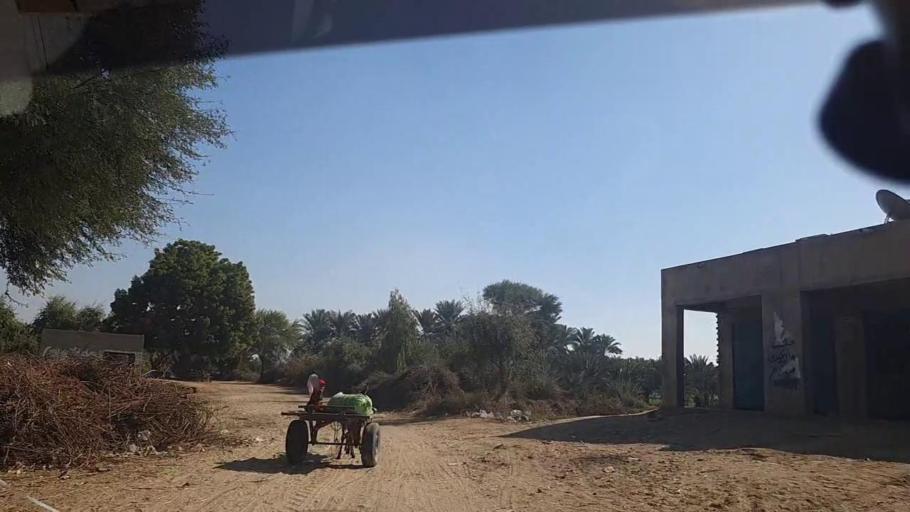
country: PK
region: Sindh
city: Khanpur
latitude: 27.6604
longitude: 69.2772
